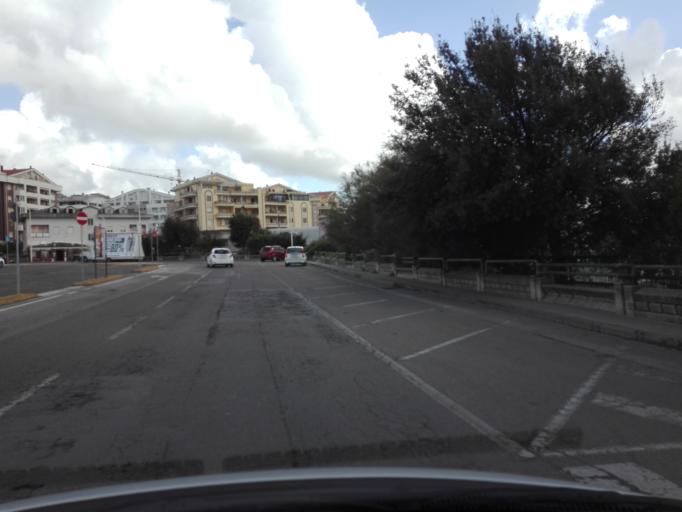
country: IT
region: Sardinia
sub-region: Provincia di Sassari
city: Sassari
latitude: 40.7174
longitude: 8.5815
